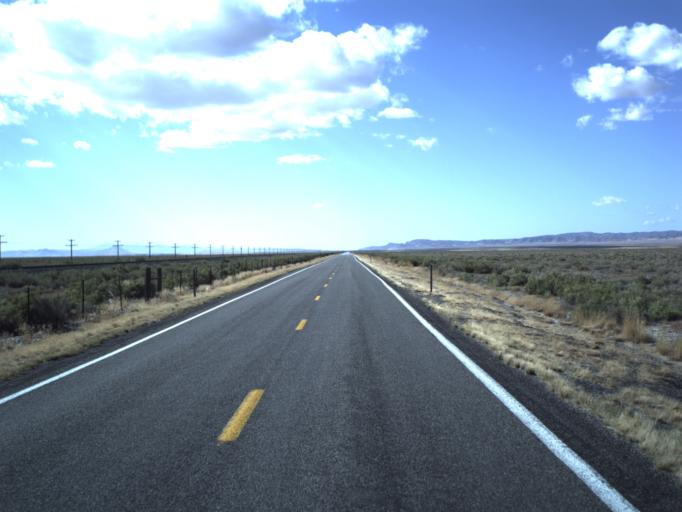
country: US
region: Utah
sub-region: Millard County
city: Delta
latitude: 39.0998
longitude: -112.7477
